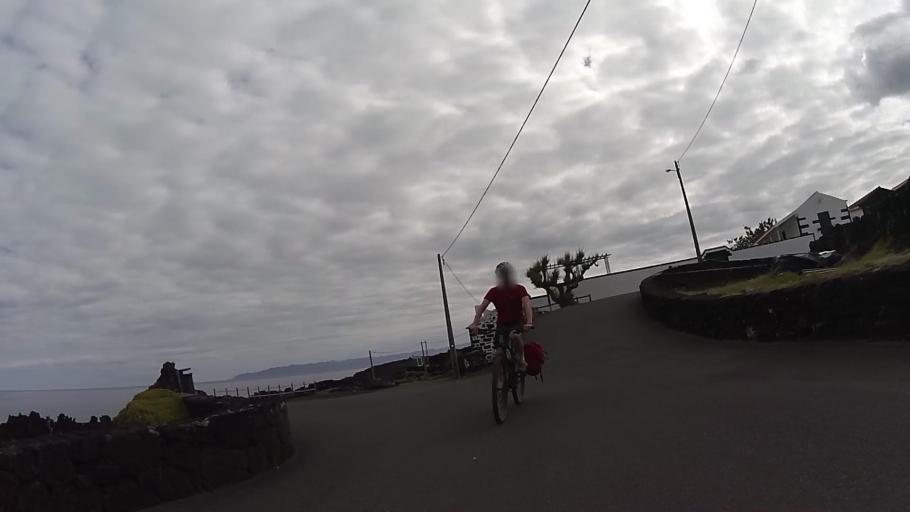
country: PT
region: Azores
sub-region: Madalena
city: Madalena
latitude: 38.5559
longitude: -28.4467
